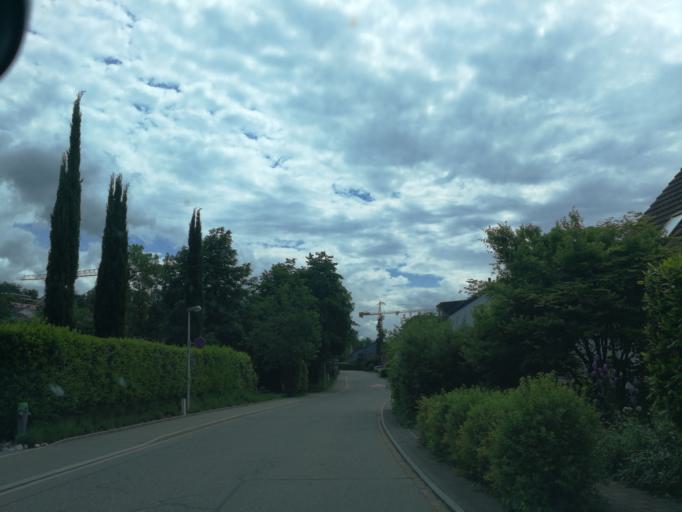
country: CH
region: Zurich
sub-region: Bezirk Meilen
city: Herrliberg
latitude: 47.2912
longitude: 8.6146
